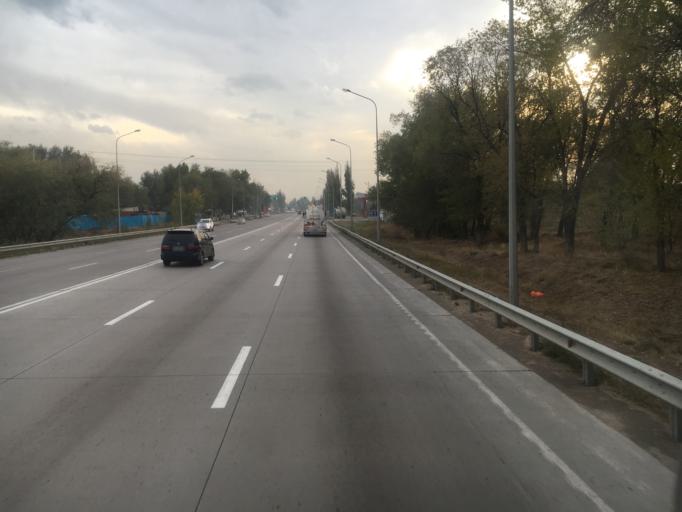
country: KZ
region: Almaty Oblysy
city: Pervomayskiy
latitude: 43.3720
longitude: 76.9515
